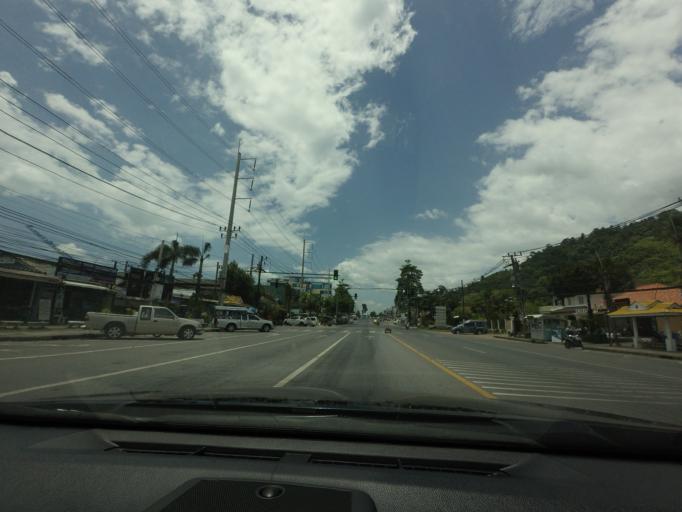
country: TH
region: Phangnga
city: Ban Khao Lak
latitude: 8.6447
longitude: 98.2516
